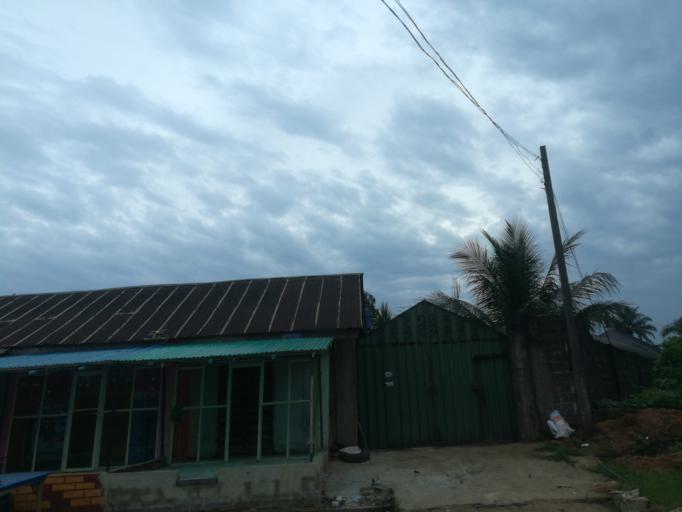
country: NG
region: Rivers
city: Port Harcourt
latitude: 4.7941
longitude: 6.9560
